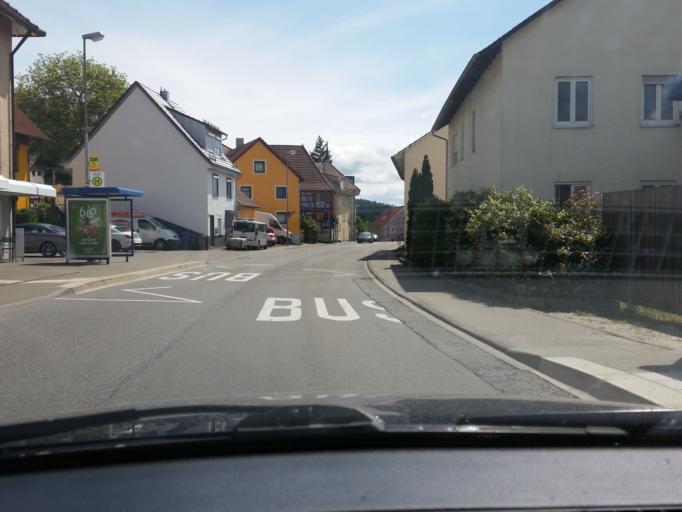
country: DE
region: Baden-Wuerttemberg
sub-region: Freiburg Region
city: Allensbach
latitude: 47.7364
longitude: 9.1166
